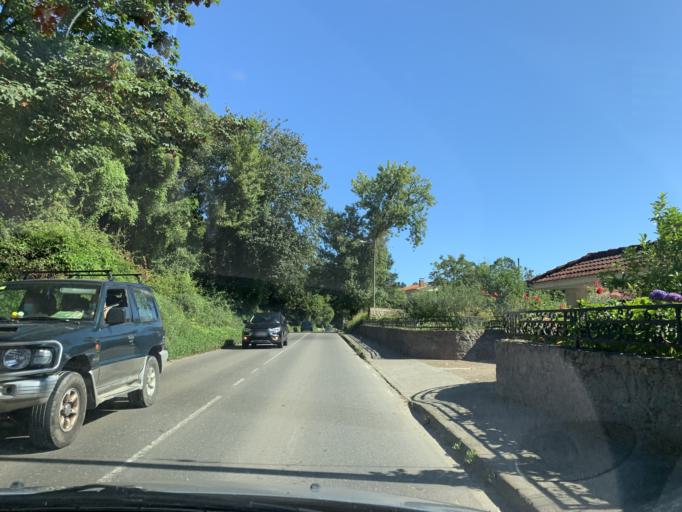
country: ES
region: Asturias
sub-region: Province of Asturias
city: Llanes
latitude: 43.4279
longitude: -4.8626
